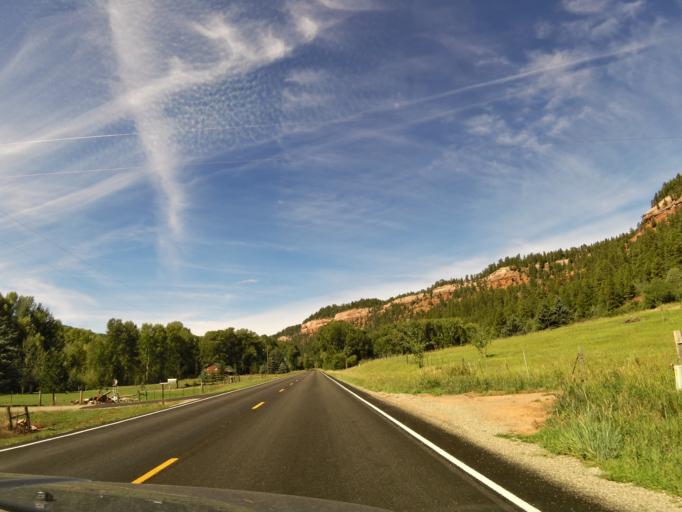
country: US
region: Colorado
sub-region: Montezuma County
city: Mancos
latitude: 37.5780
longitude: -108.2237
